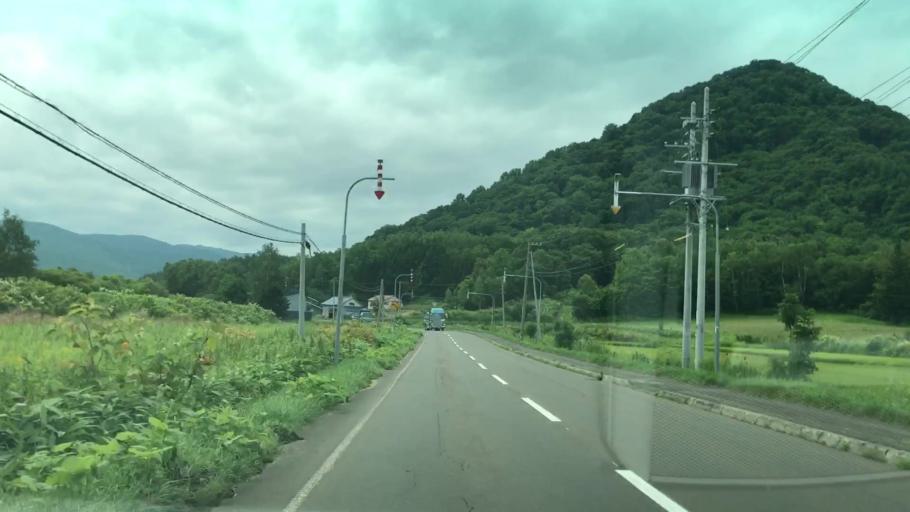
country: JP
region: Hokkaido
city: Yoichi
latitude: 43.0742
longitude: 140.8165
